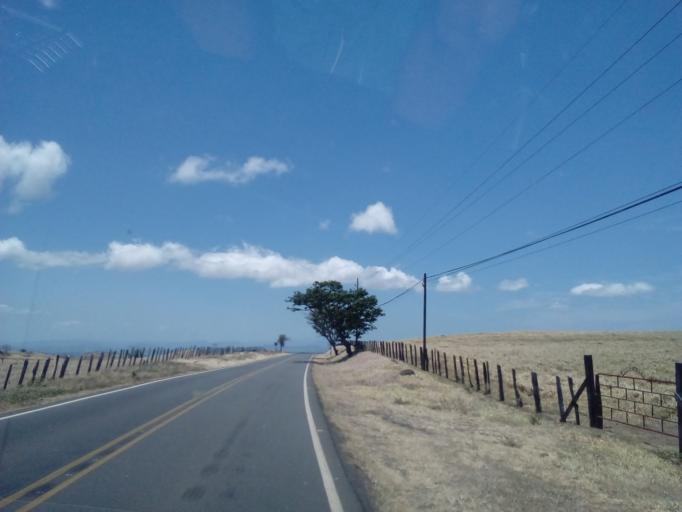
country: CR
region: Guanacaste
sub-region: Canton de Tilaran
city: Tilaran
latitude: 10.4886
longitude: -85.0236
